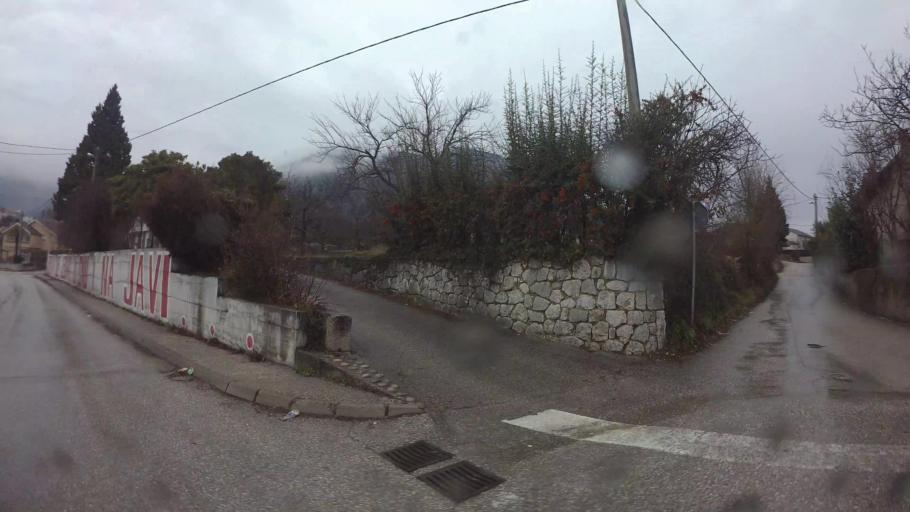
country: BA
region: Federation of Bosnia and Herzegovina
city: Cim
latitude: 43.3520
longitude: 17.7803
